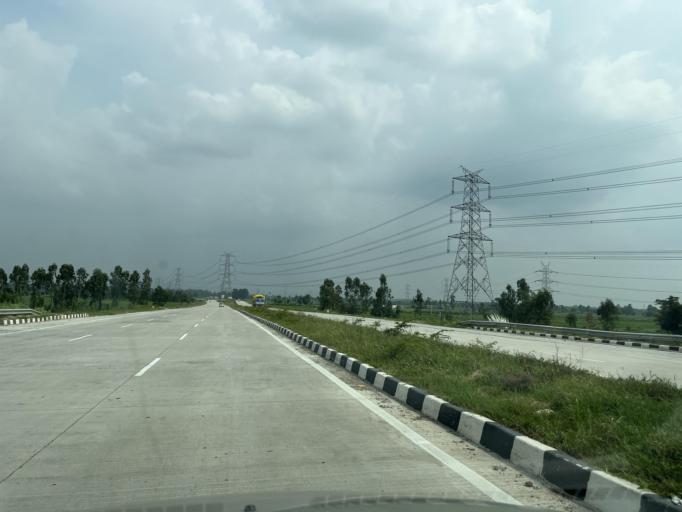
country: IN
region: Uttarakhand
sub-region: Udham Singh Nagar
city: Jaspur
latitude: 29.2874
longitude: 78.8549
